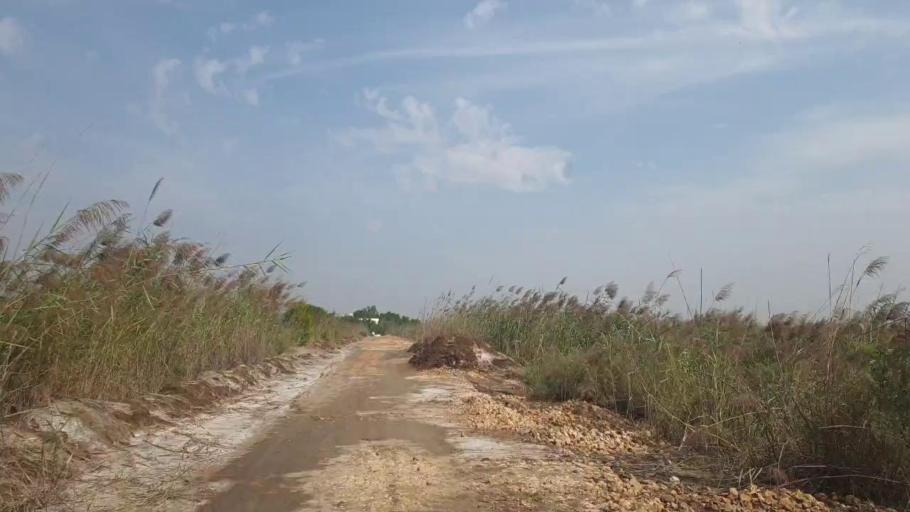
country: PK
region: Sindh
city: Rajo Khanani
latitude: 24.9978
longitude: 69.0022
